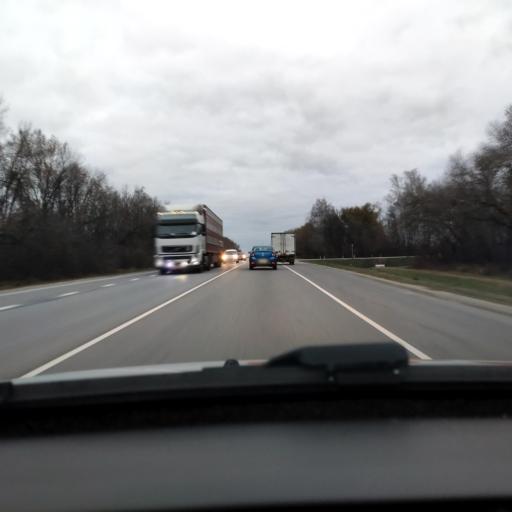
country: RU
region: Lipetsk
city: Borinskoye
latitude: 52.3907
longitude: 39.2286
